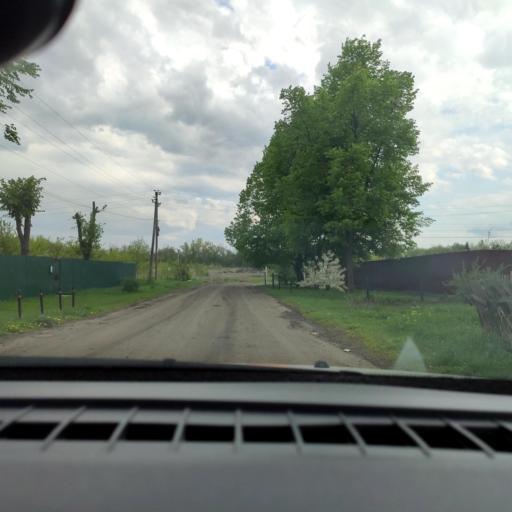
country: RU
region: Voronezj
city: Maslovka
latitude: 51.5339
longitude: 39.3381
